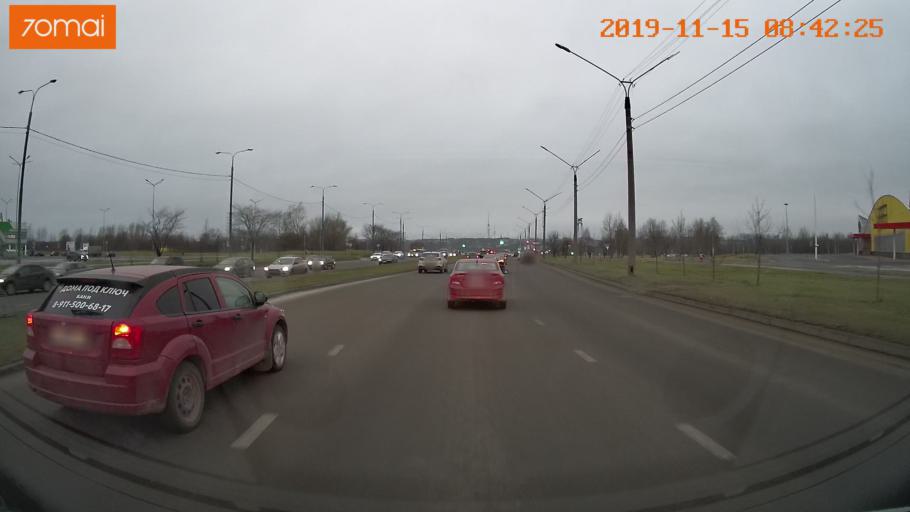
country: RU
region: Vologda
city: Cherepovets
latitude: 59.1028
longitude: 37.9081
